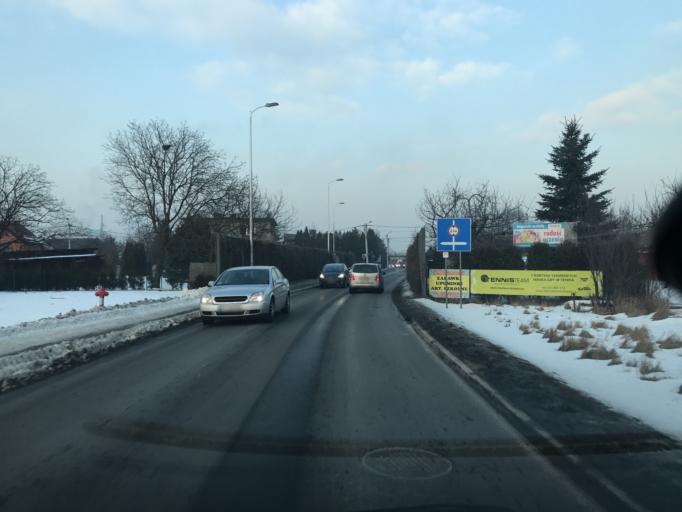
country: PL
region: Silesian Voivodeship
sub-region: Tychy
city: Tychy
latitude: 50.1245
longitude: 18.9678
